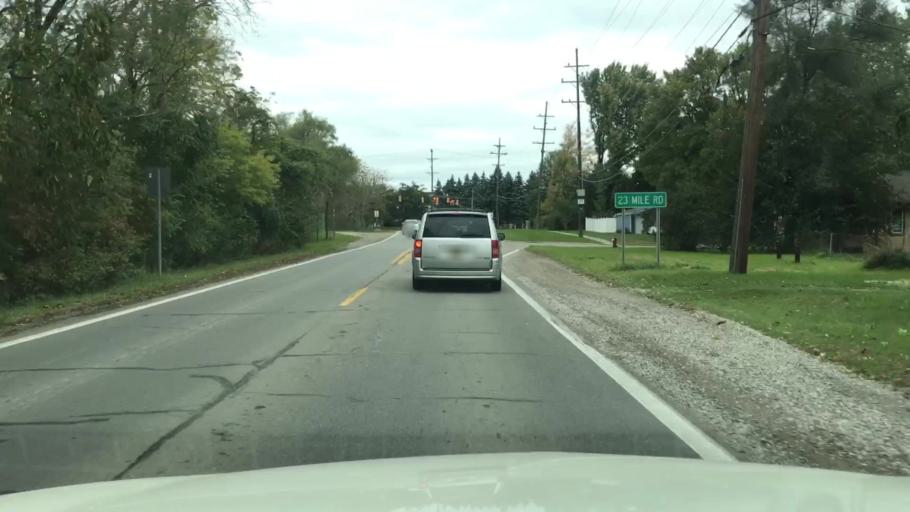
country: US
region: Michigan
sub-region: Macomb County
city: Shelby
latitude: 42.6666
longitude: -83.0736
